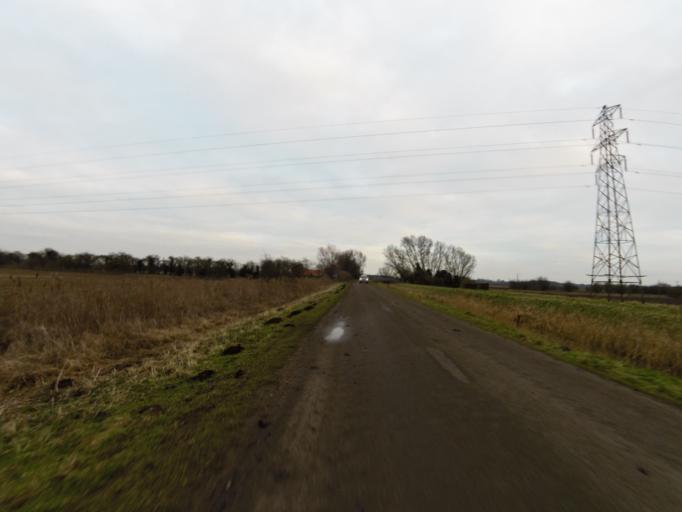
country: GB
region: England
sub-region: Cambridgeshire
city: Waterbeach
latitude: 52.2543
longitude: 0.2312
